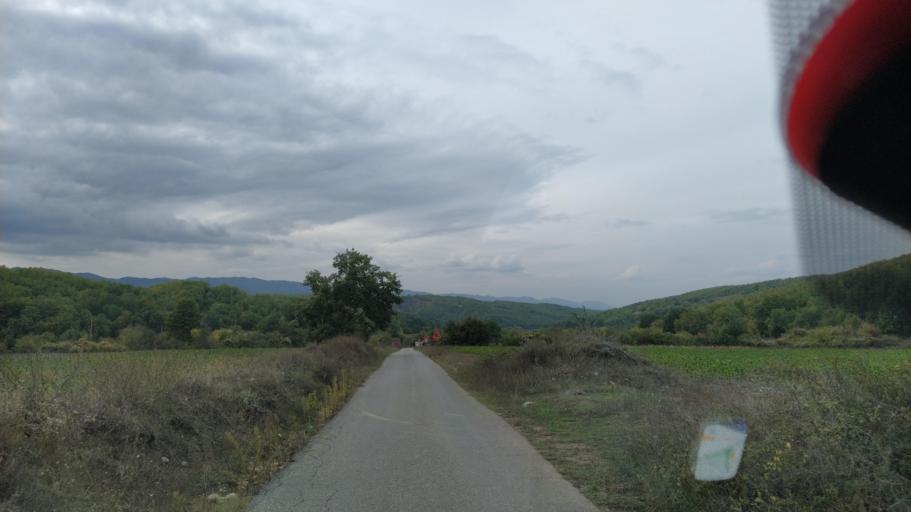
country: MK
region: Konce
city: Konce
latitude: 41.5070
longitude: 22.4671
